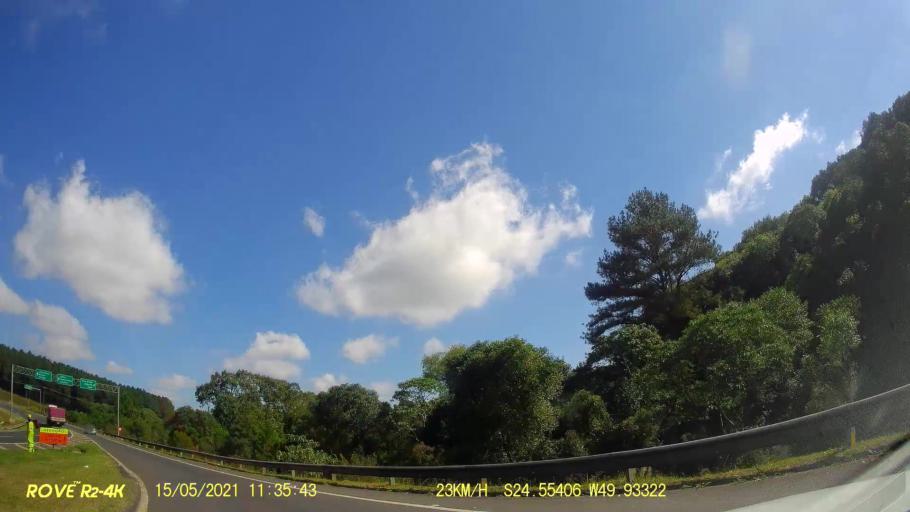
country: BR
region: Parana
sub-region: Pirai Do Sul
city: Pirai do Sul
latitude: -24.5543
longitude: -49.9338
